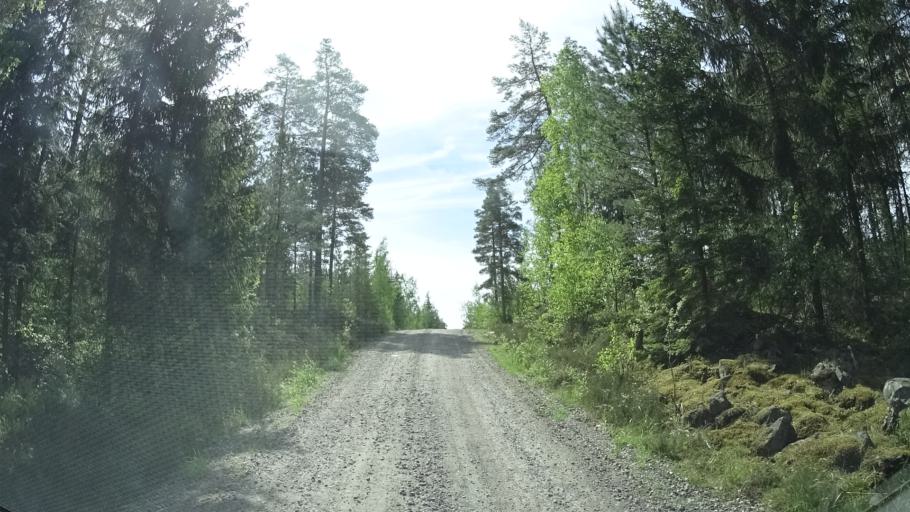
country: SE
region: OEstergoetland
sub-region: Finspangs Kommun
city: Finspang
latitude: 58.7827
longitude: 15.8466
